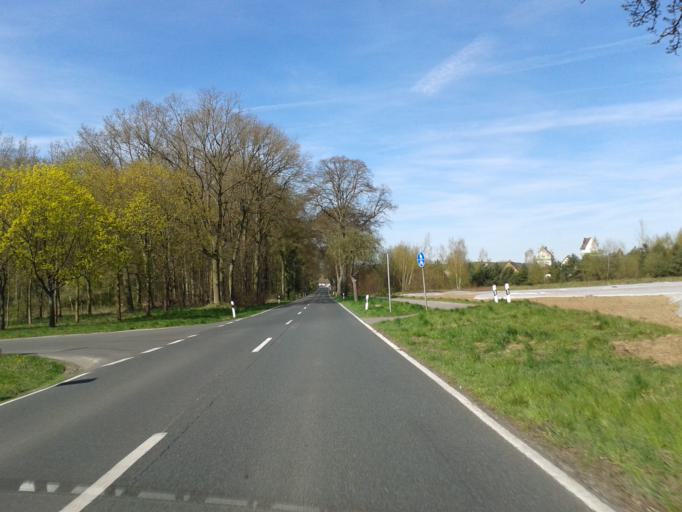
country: DE
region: Lower Saxony
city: Clenze
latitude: 52.9366
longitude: 10.9679
